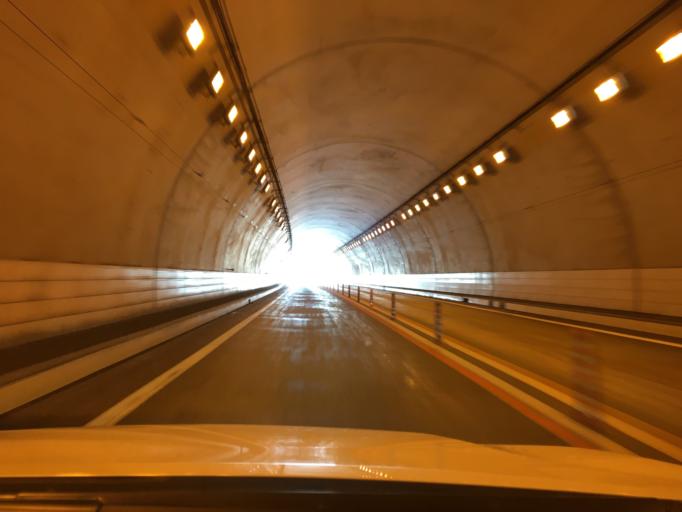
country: JP
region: Yamagata
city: Sagae
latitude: 38.4461
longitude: 140.0202
